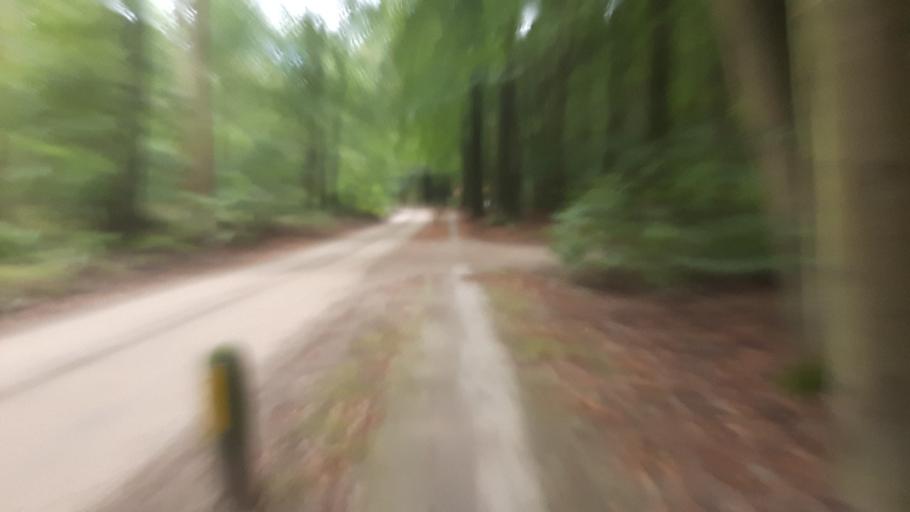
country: NL
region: Gelderland
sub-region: Gemeente Ermelo
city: Ermelo
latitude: 52.2743
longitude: 5.6276
